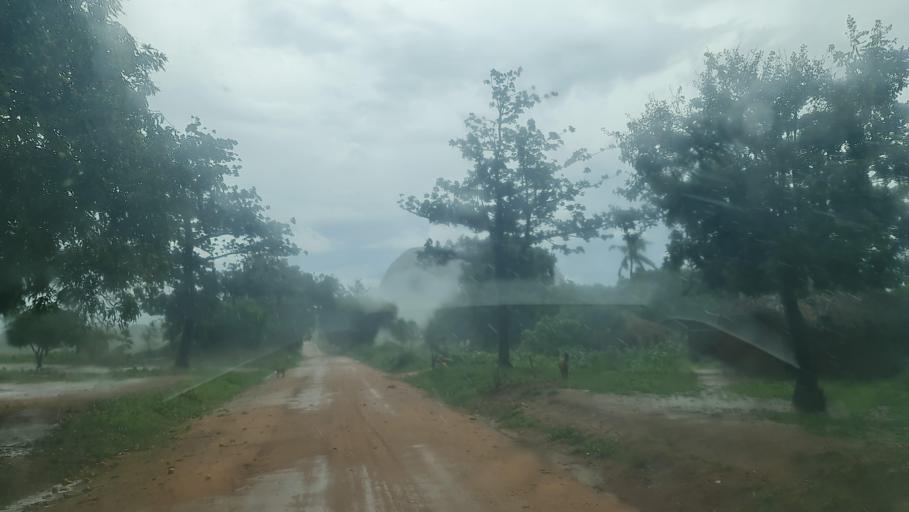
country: MW
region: Southern Region
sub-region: Nsanje District
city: Nsanje
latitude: -17.4022
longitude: 35.5937
